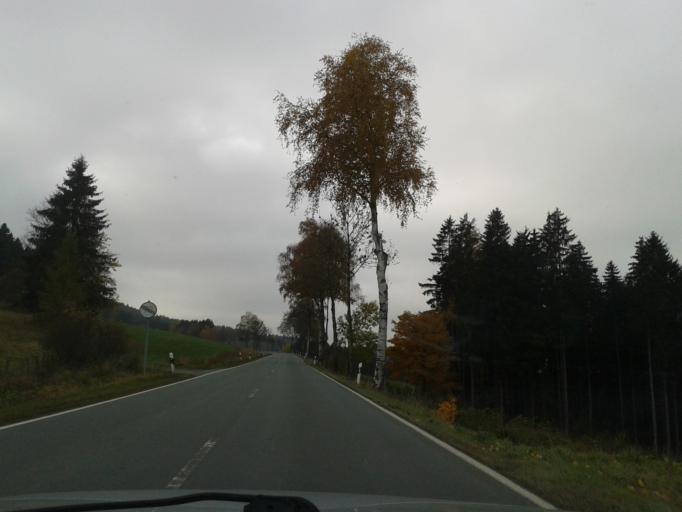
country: DE
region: North Rhine-Westphalia
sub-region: Regierungsbezirk Arnsberg
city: Bad Berleburg
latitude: 50.9879
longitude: 8.3503
